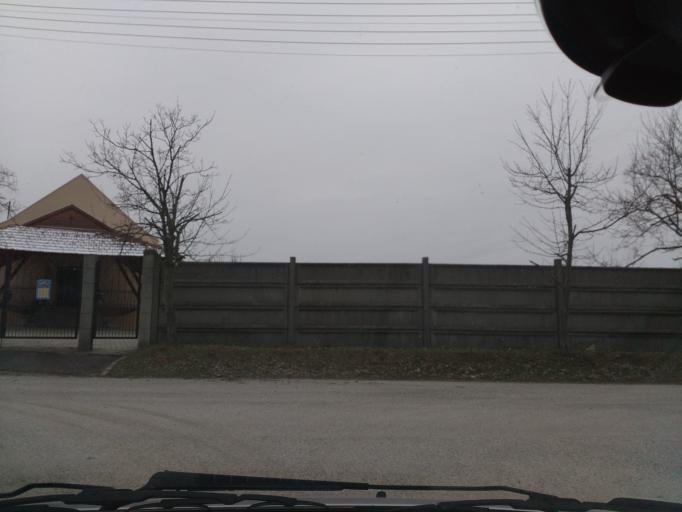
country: HU
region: Komarom-Esztergom
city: Piliscsev
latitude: 47.6690
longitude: 18.8162
